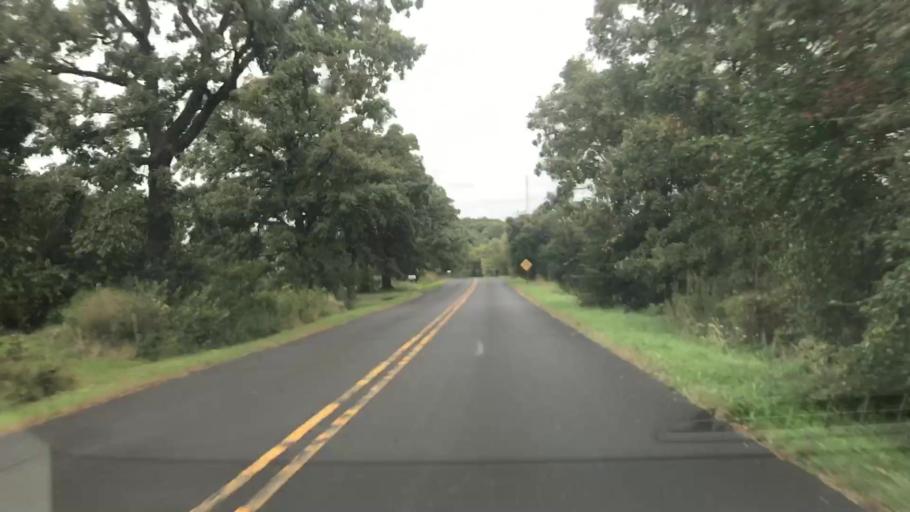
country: US
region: Wisconsin
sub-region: Waukesha County
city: North Prairie
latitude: 42.9151
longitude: -88.4104
